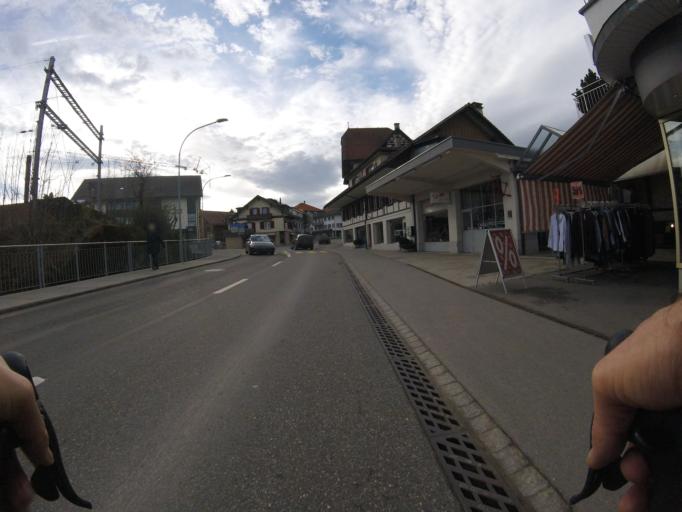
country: CH
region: Bern
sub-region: Bern-Mittelland District
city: Wahlern
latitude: 46.8188
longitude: 7.3410
